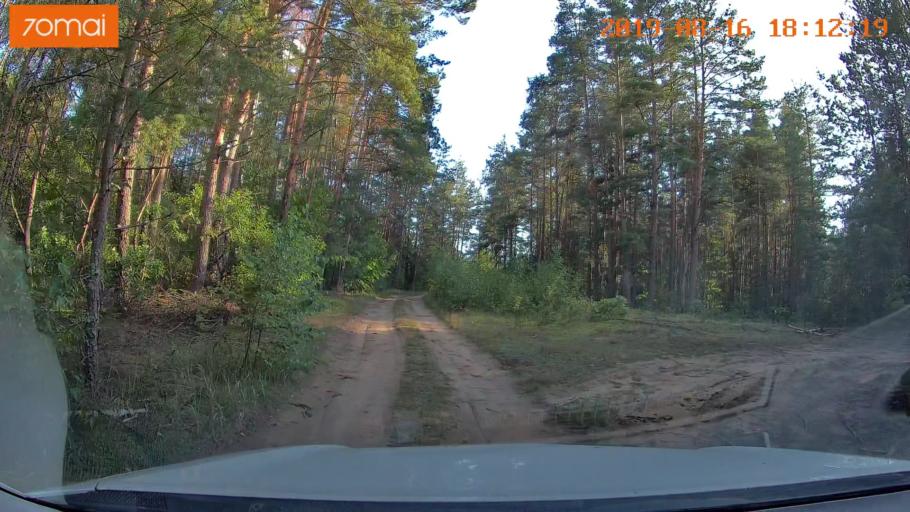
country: BY
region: Mogilev
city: Asipovichy
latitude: 53.2134
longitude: 28.6454
